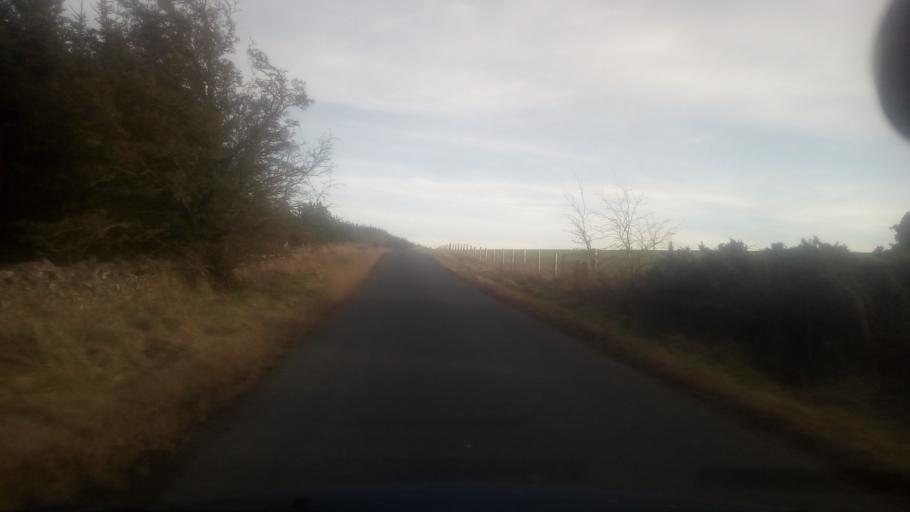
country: GB
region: Scotland
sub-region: The Scottish Borders
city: Jedburgh
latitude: 55.4019
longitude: -2.5989
